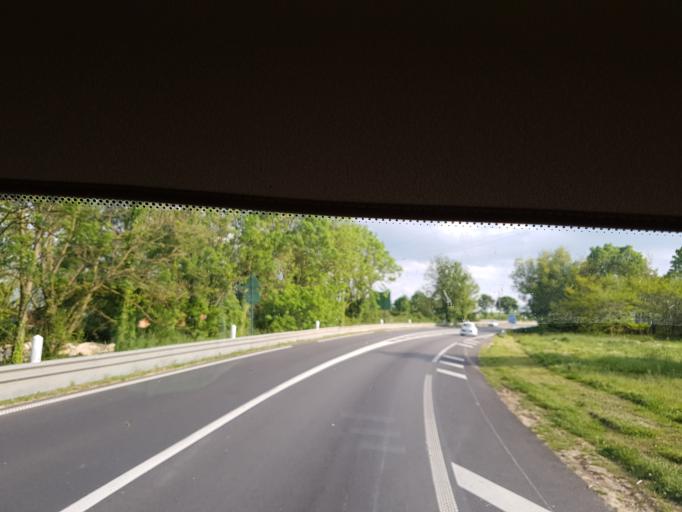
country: FR
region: Nord-Pas-de-Calais
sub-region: Departement du Pas-de-Calais
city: Hesdin
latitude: 50.3632
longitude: 2.0389
